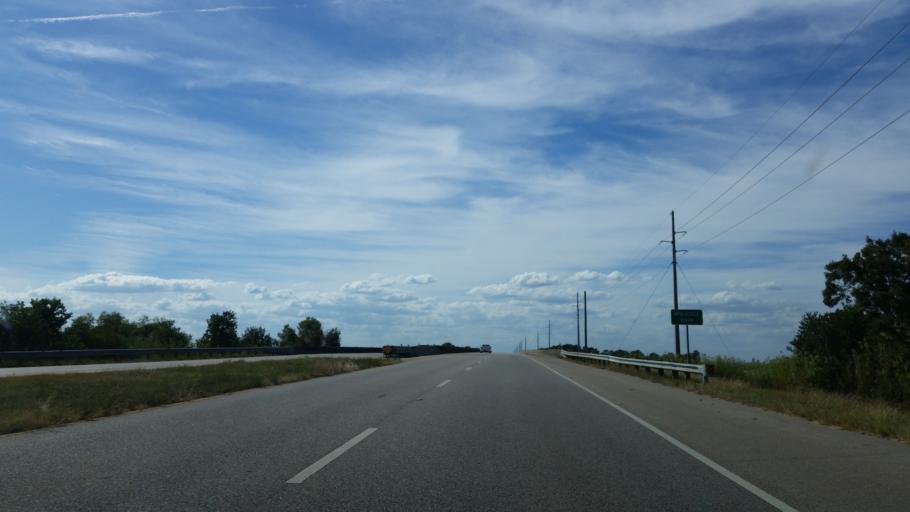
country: US
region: Alabama
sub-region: Baldwin County
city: Spanish Fort
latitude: 30.6720
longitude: -87.9490
